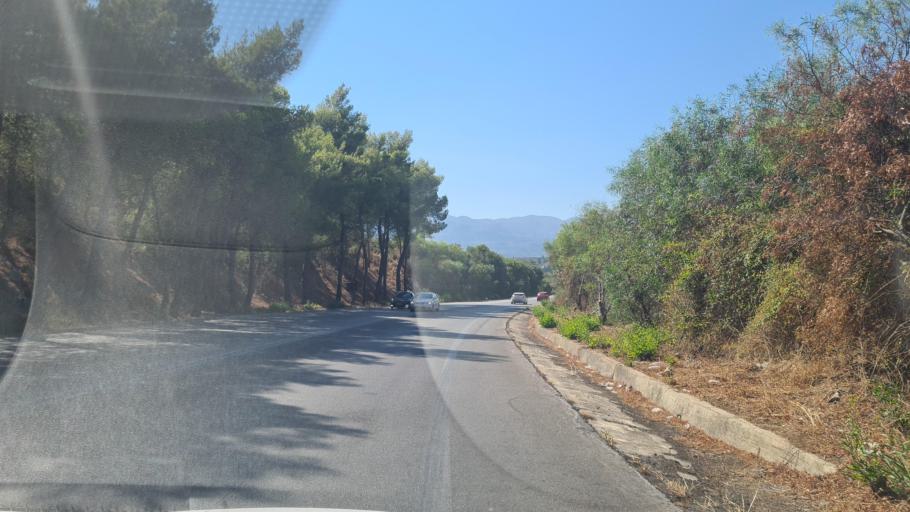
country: GR
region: Crete
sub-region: Nomos Chanias
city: Kalivai
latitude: 35.4060
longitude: 24.1493
